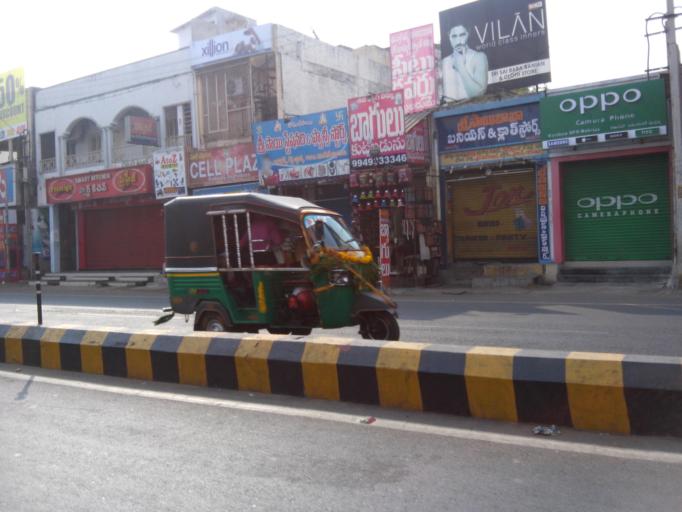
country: IN
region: Andhra Pradesh
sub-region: Krishna
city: Vijayawada
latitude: 16.5145
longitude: 80.6337
